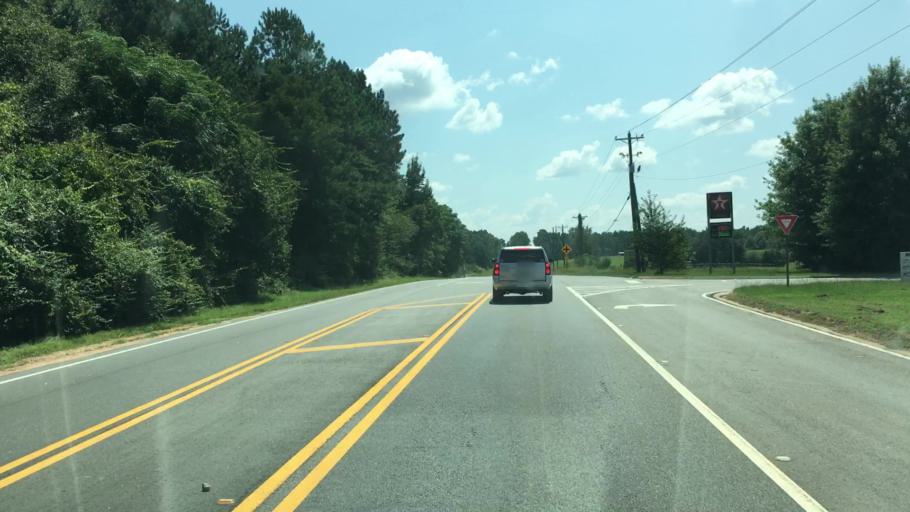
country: US
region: Georgia
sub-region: Oconee County
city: Watkinsville
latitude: 33.7793
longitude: -83.4244
